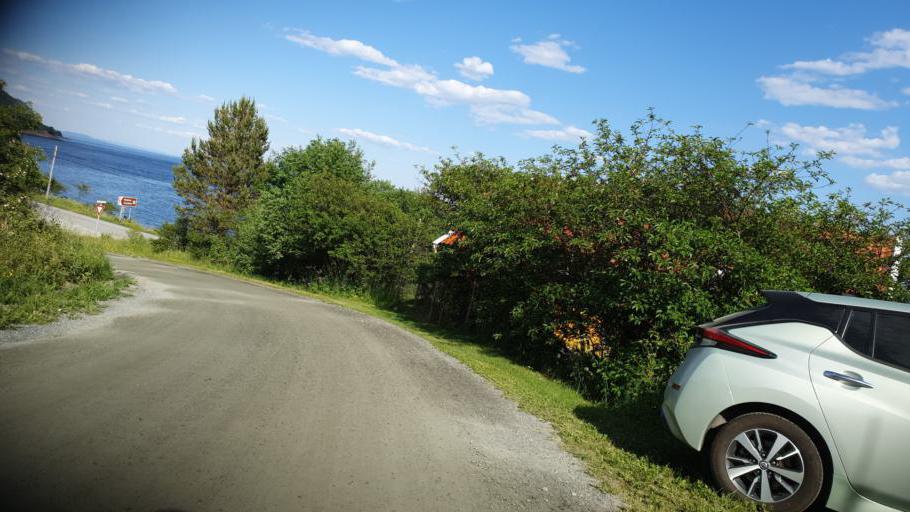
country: NO
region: Sor-Trondelag
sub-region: Trondheim
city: Trondheim
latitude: 63.5821
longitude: 10.4165
